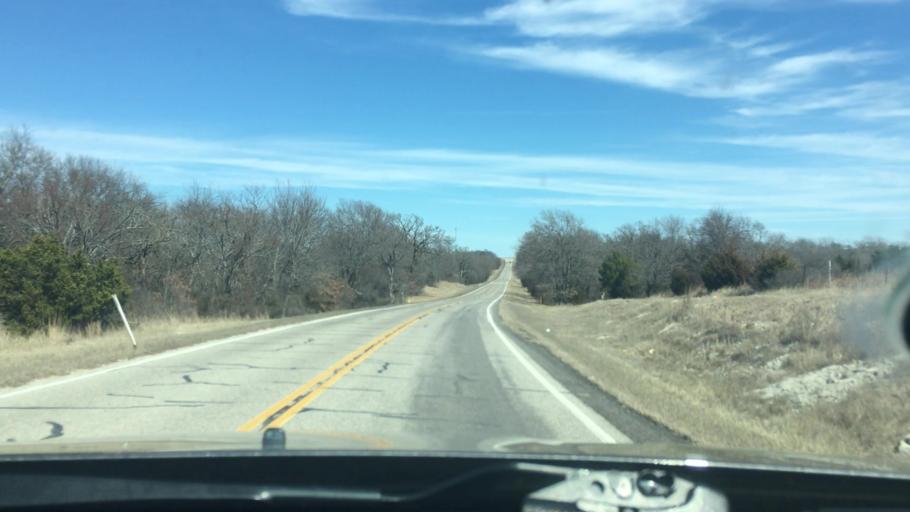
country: US
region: Oklahoma
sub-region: Carter County
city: Dickson
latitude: 34.3223
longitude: -96.9597
